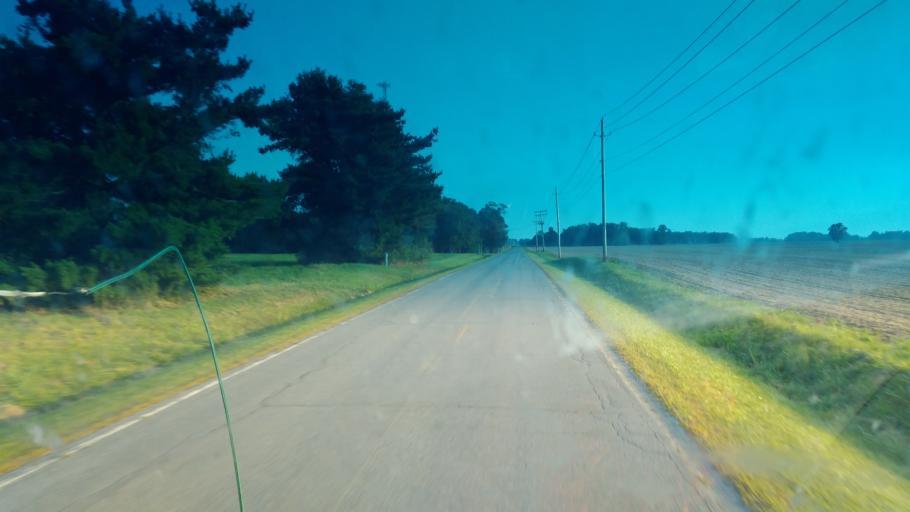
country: US
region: Ohio
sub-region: Crawford County
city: Crestline
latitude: 40.8211
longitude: -82.8188
